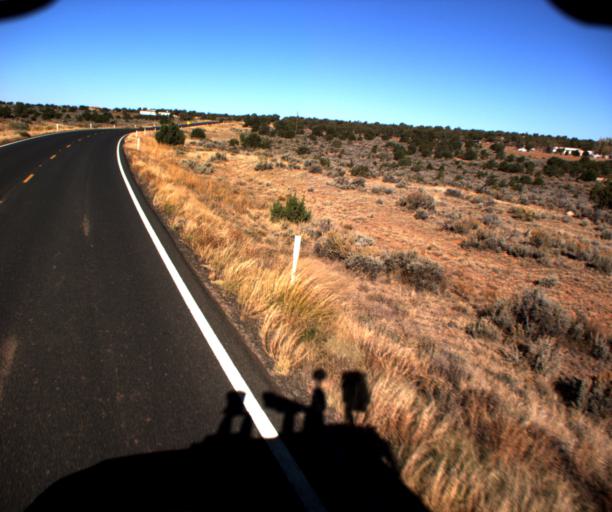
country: US
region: Arizona
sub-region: Apache County
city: Ganado
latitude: 35.7614
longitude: -109.7812
